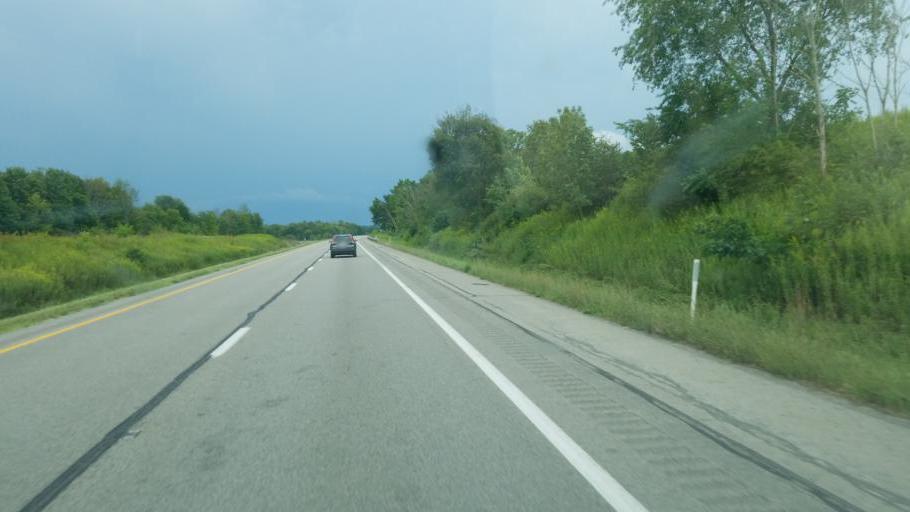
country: US
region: Pennsylvania
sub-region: Mercer County
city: Stoneboro
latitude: 41.3078
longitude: -80.1585
